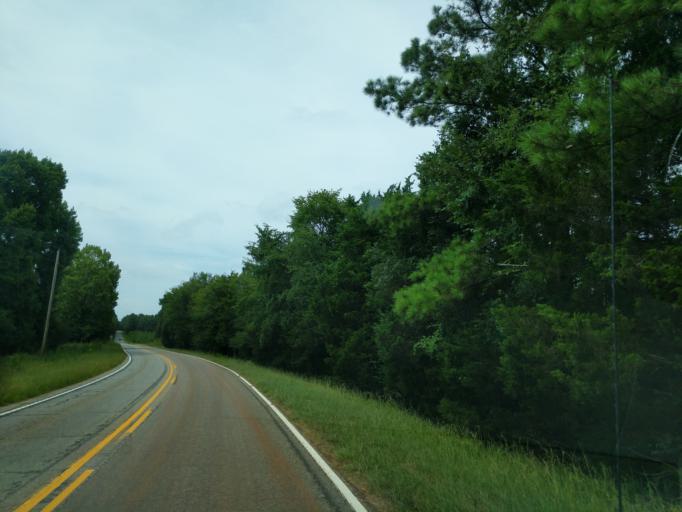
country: US
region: South Carolina
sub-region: Abbeville County
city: Calhoun Falls
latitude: 34.1304
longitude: -82.5914
